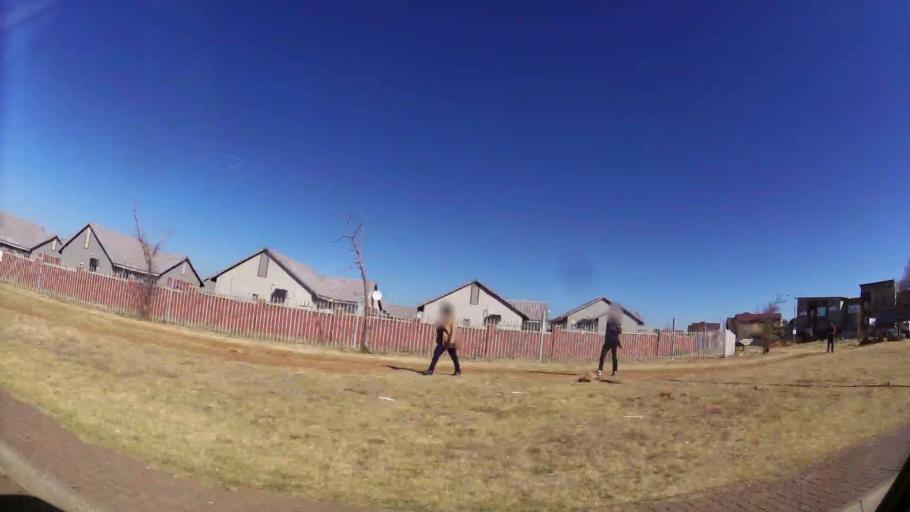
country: ZA
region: Gauteng
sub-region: City of Johannesburg Metropolitan Municipality
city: Johannesburg
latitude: -26.2901
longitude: 28.0900
